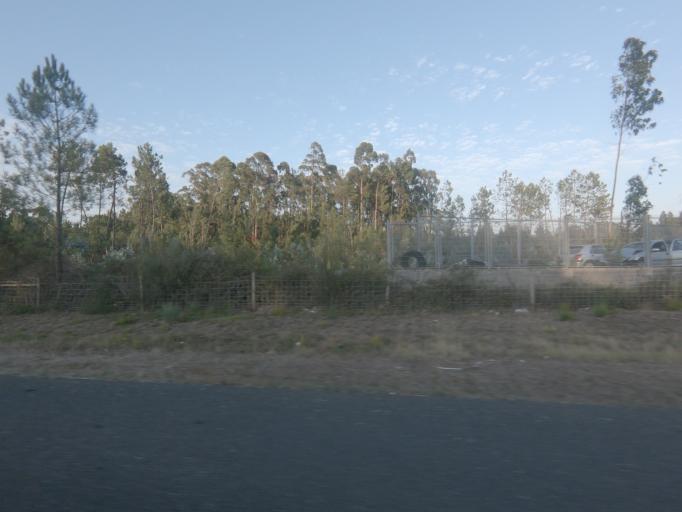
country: PT
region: Santarem
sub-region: Ourem
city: Fatima
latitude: 39.6298
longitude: -8.6979
